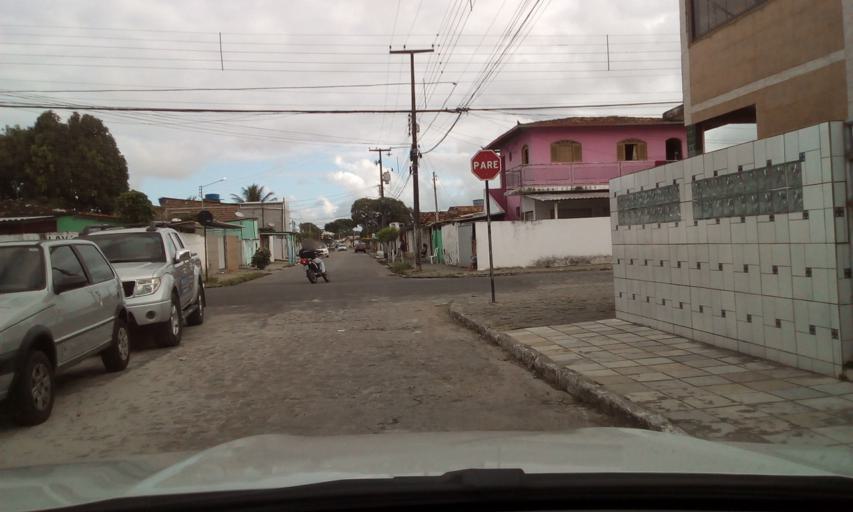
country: BR
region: Paraiba
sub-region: Joao Pessoa
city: Joao Pessoa
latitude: -7.1471
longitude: -34.8773
